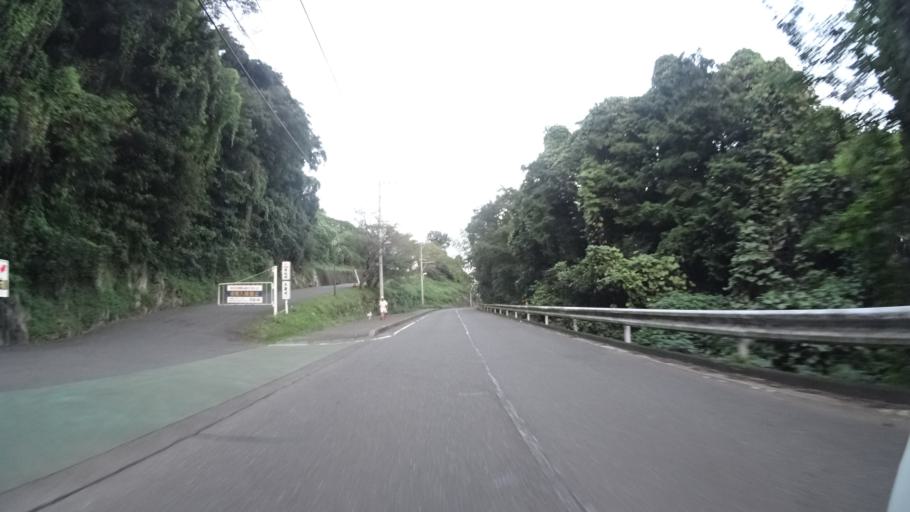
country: JP
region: Oita
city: Beppu
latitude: 33.3189
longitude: 131.4824
